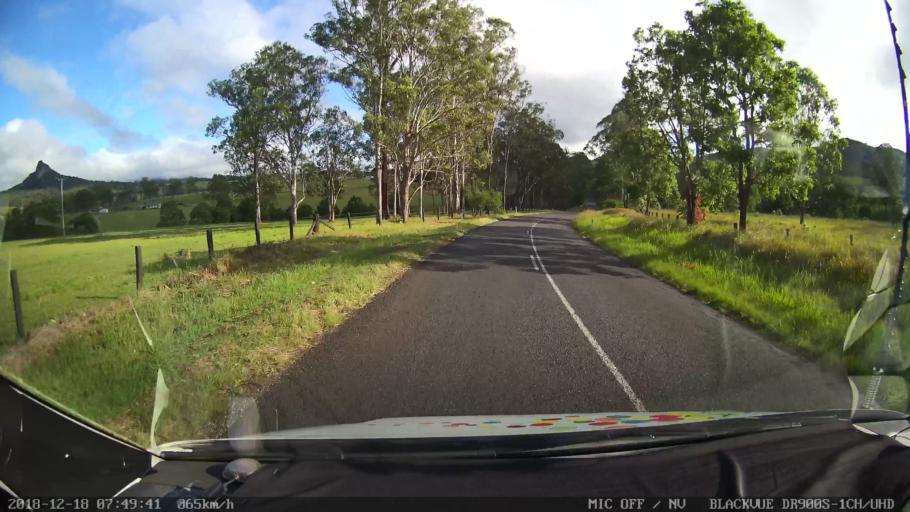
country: AU
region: New South Wales
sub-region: Kyogle
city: Kyogle
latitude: -28.4517
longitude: 152.5704
